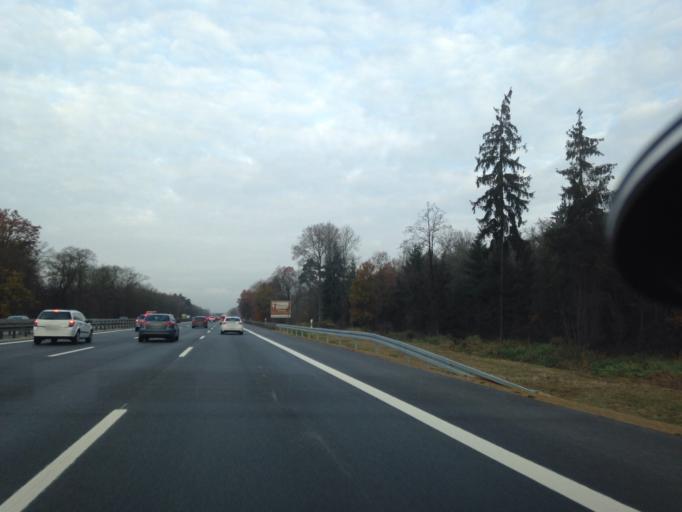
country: DE
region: Bavaria
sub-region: Regierungsbezirk Mittelfranken
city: Wetzendorf
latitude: 49.5181
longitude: 11.0827
